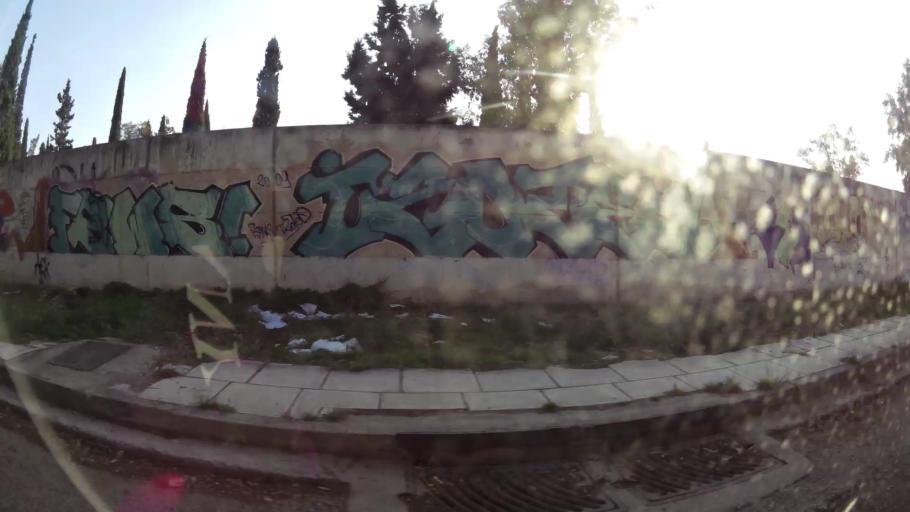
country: GR
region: Attica
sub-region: Nomarchia Athinas
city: Nea Filadelfeia
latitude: 38.0491
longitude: 23.7348
